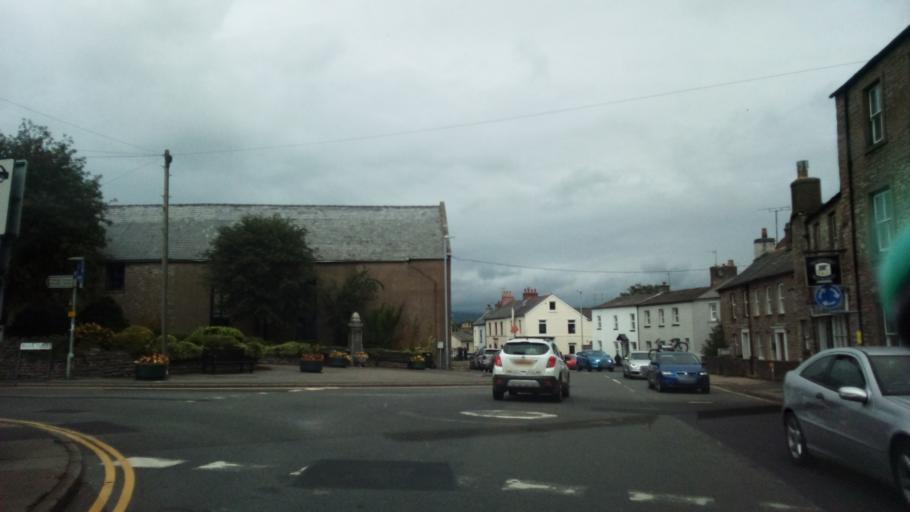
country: GB
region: England
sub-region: Cumbria
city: Kirkby Stephen
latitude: 54.4743
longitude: -2.3491
